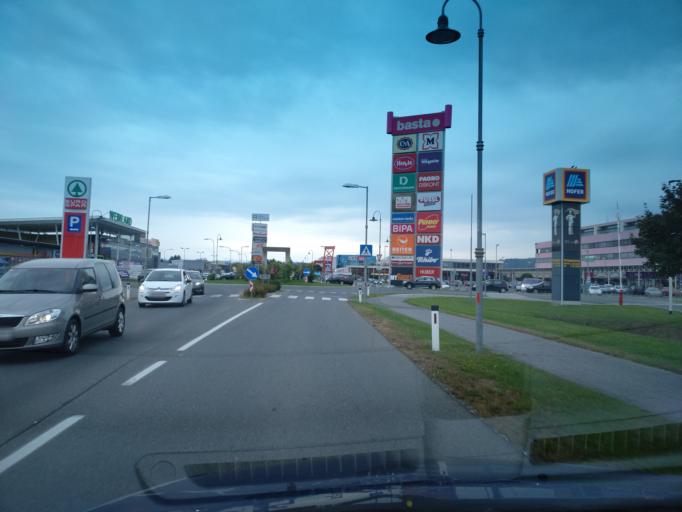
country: AT
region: Styria
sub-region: Politischer Bezirk Leibnitz
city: Kaindorf an der Sulm
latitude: 46.7964
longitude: 15.5571
